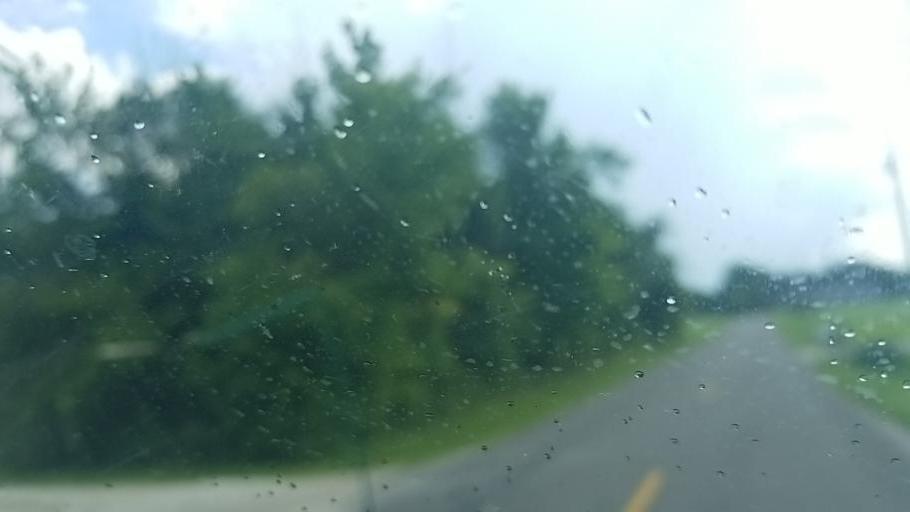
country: US
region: Ohio
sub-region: Medina County
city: Lodi
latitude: 41.1455
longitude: -81.9945
